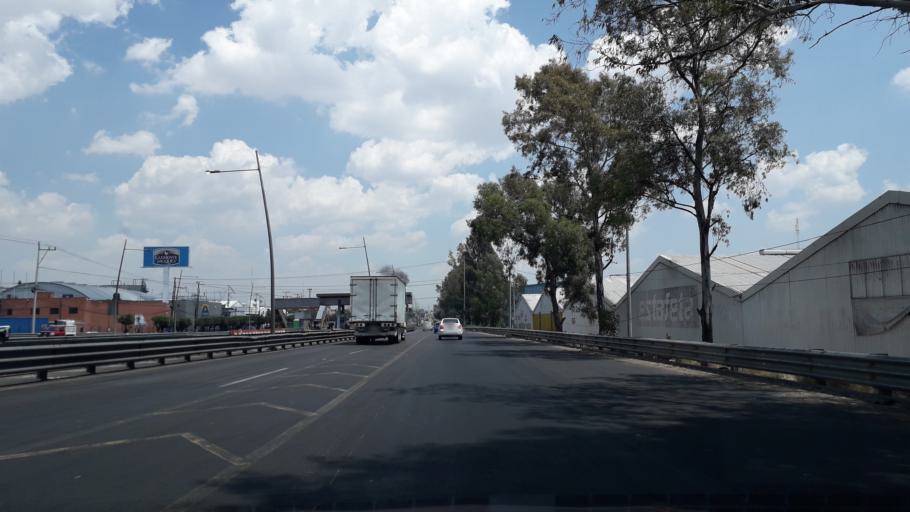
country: MX
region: Puebla
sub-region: Puebla
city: San Sebastian de Aparicio
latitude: 19.0773
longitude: -98.1517
